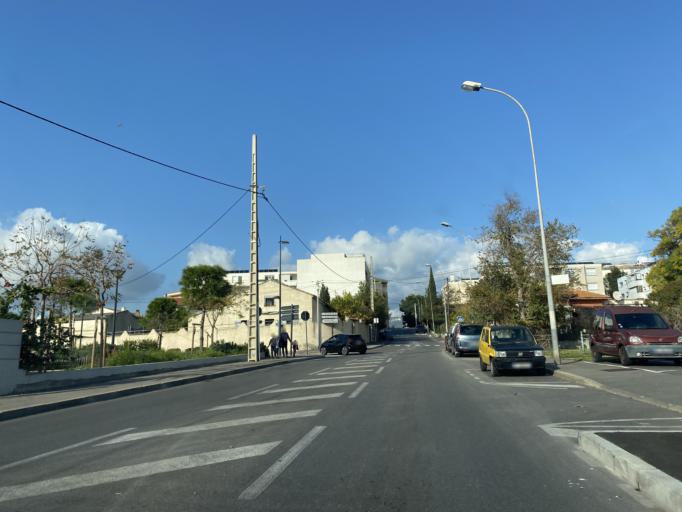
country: FR
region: Provence-Alpes-Cote d'Azur
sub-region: Departement du Var
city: La Seyne-sur-Mer
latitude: 43.1110
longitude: 5.8731
